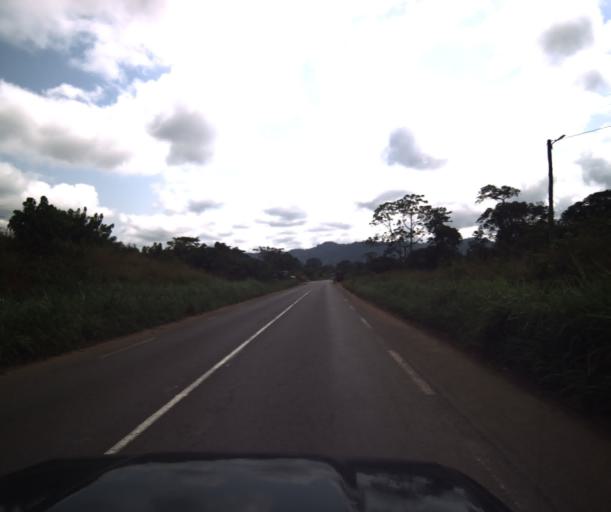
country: CM
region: Centre
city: Eseka
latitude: 3.8898
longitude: 10.7134
